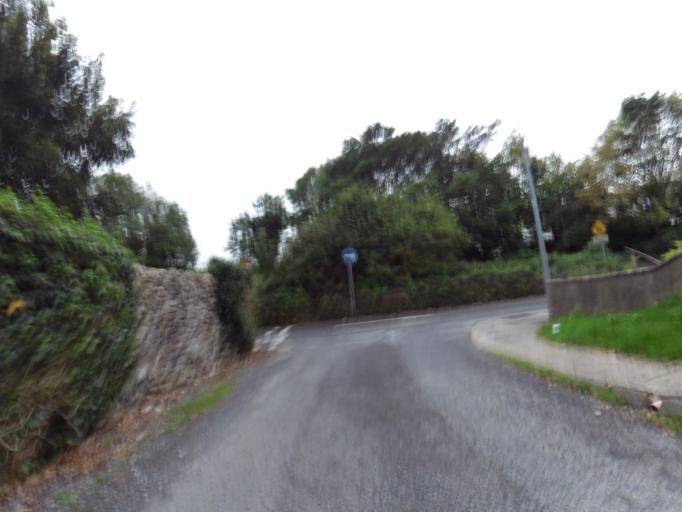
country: IE
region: Connaught
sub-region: County Galway
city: Loughrea
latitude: 53.1992
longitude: -8.5627
